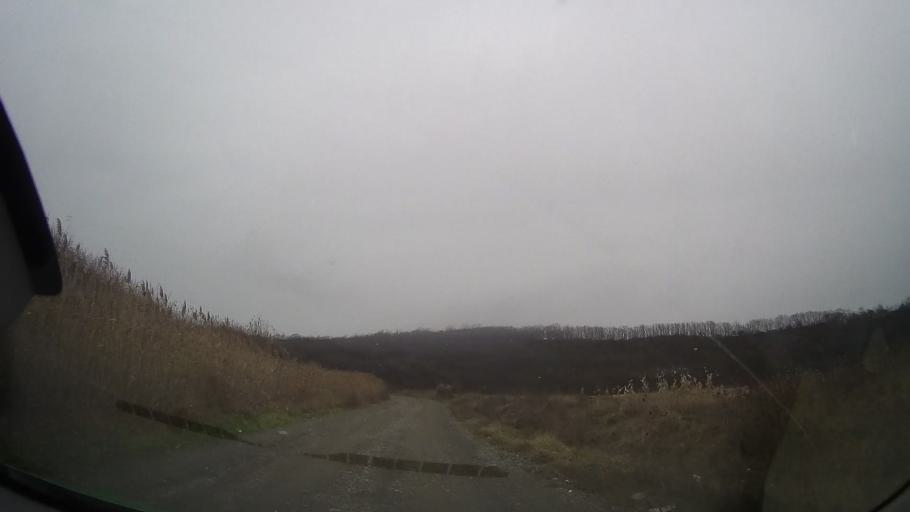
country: RO
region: Mures
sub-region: Comuna Ceausu de Campie
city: Ceausu de Campie
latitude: 46.6504
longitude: 24.4974
